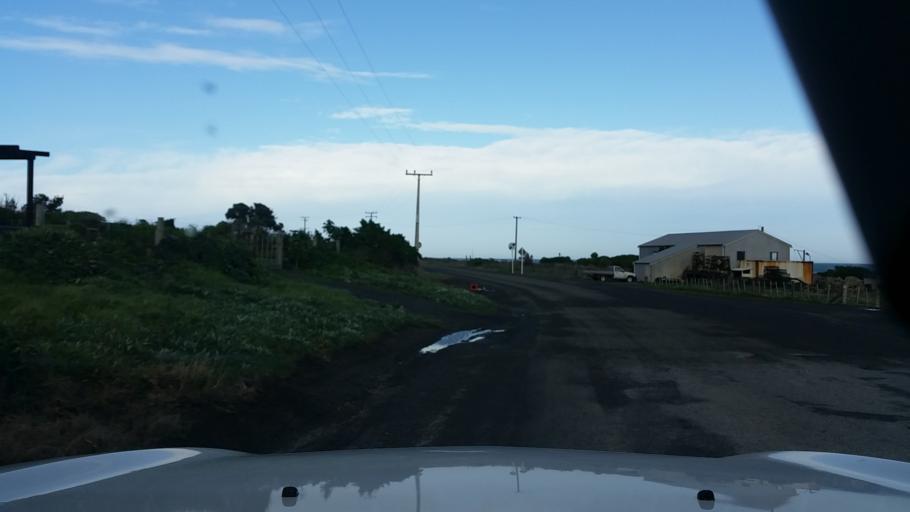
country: NZ
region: Wellington
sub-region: South Wairarapa District
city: Waipawa
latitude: -41.5895
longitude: 175.2335
